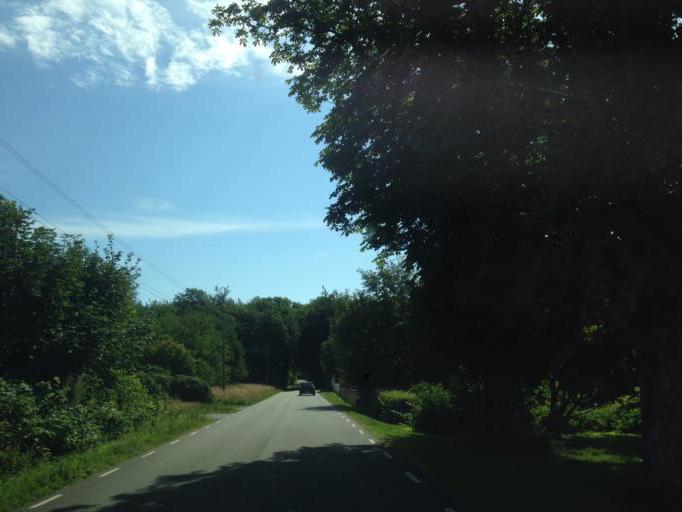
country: SE
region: Skane
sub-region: Simrishamns Kommun
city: Kivik
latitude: 55.6342
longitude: 14.1616
